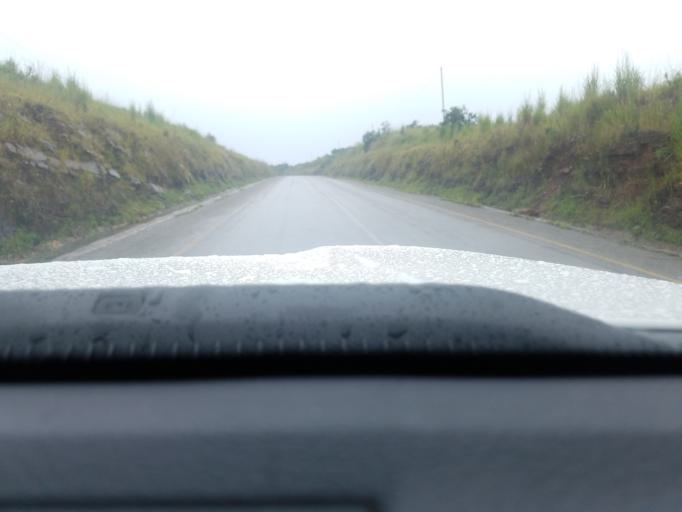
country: TZ
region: Kigoma
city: Mwandiga
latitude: -4.6616
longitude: 29.7237
